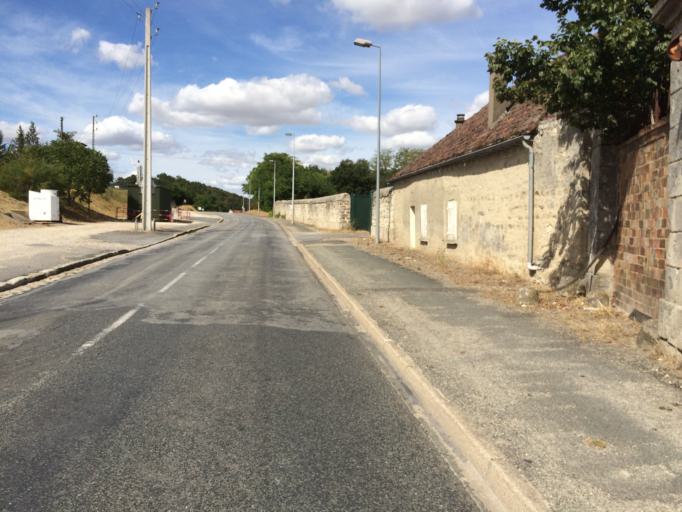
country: FR
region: Ile-de-France
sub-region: Departement de l'Essonne
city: Maisse
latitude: 48.3965
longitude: 2.3760
